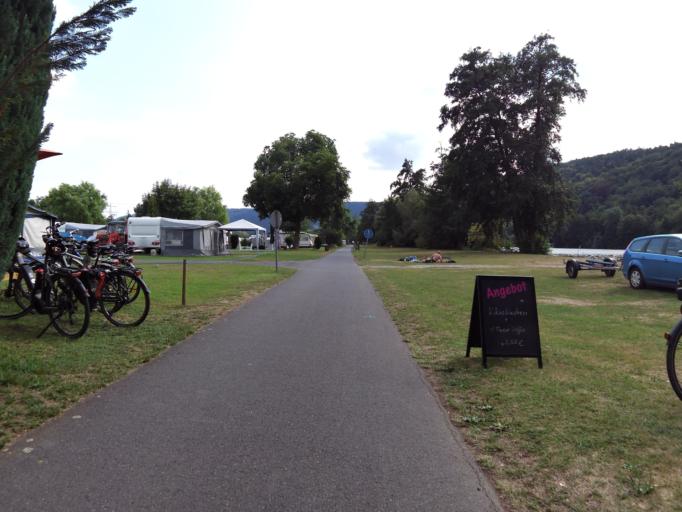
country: DE
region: Bavaria
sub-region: Regierungsbezirk Unterfranken
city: Laudenbach
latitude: 49.7607
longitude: 9.1794
